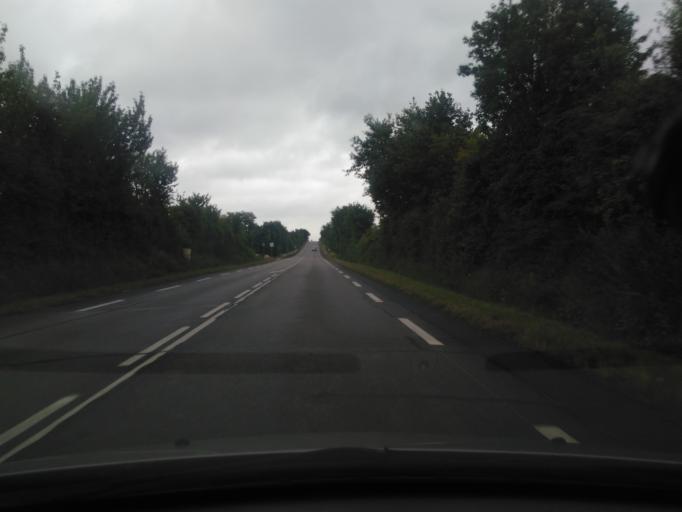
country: FR
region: Pays de la Loire
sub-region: Departement de la Vendee
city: Saint-Florent-des-Bois
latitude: 46.5862
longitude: -1.3045
